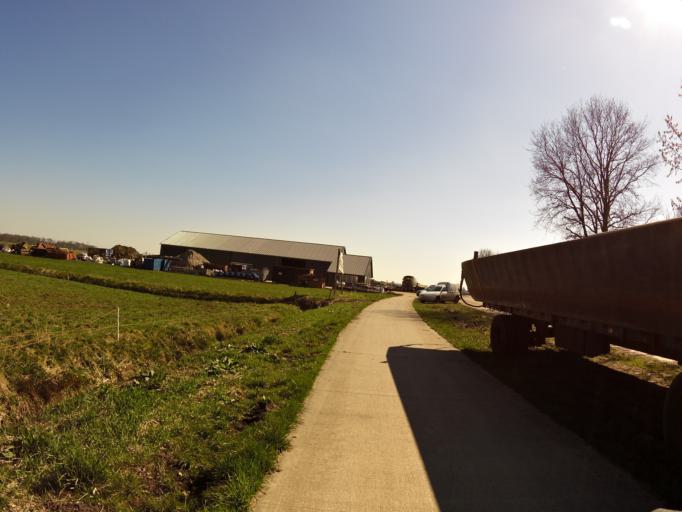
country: NL
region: Overijssel
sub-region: Gemeente Steenwijkerland
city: Blokzijl
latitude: 52.7613
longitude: 5.9950
